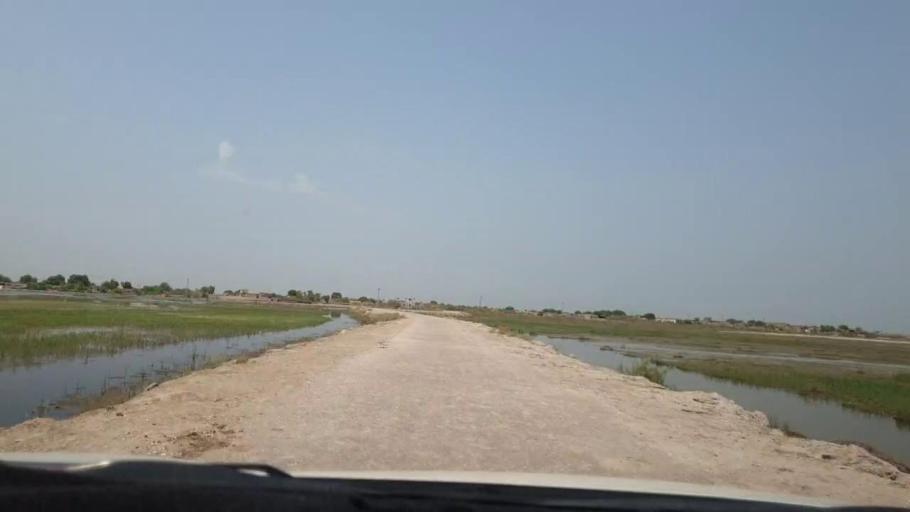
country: PK
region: Sindh
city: Radhan
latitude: 27.2456
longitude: 67.9953
